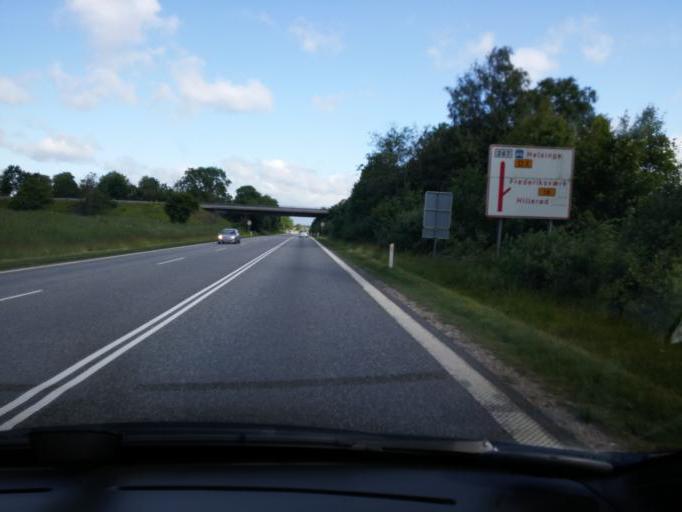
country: DK
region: Capital Region
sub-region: Hillerod Kommune
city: Hillerod
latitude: 55.9269
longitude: 12.2548
